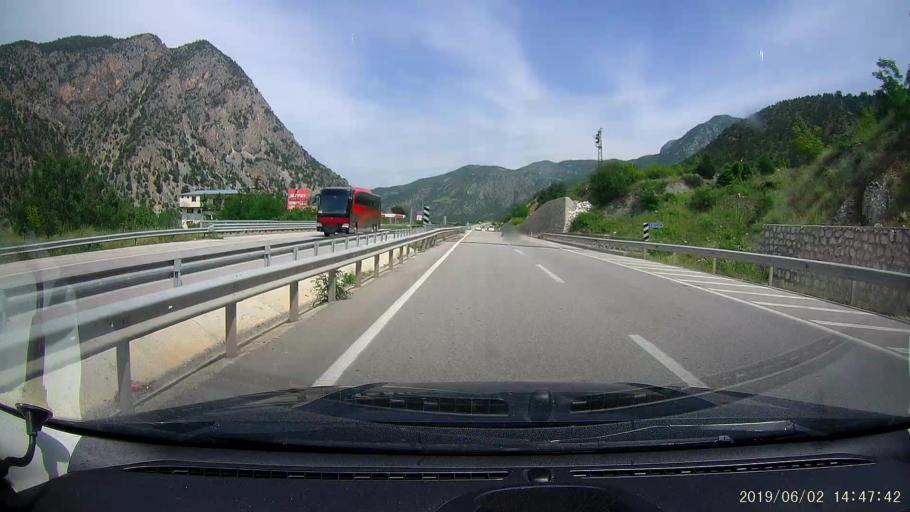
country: TR
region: Corum
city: Hacihamza
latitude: 41.0662
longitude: 34.4662
